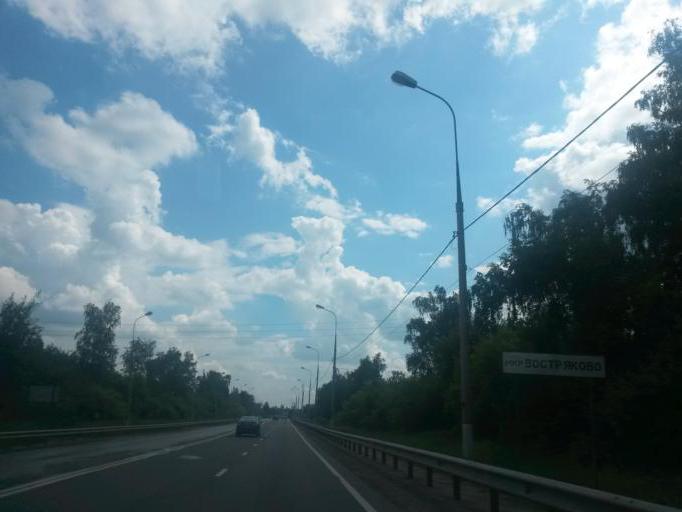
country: RU
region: Moskovskaya
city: Vostryakovo
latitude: 55.3999
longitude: 37.7870
